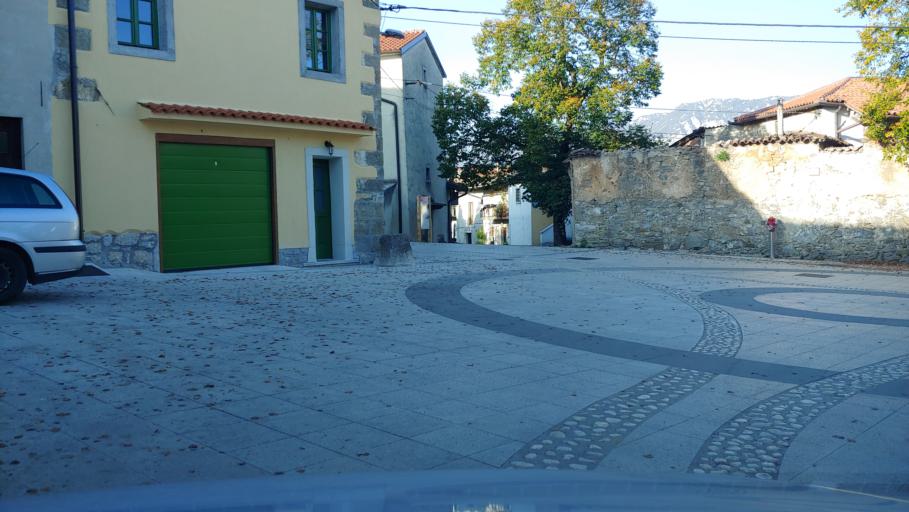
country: SI
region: Vipava
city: Vipava
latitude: 45.8396
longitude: 13.9332
